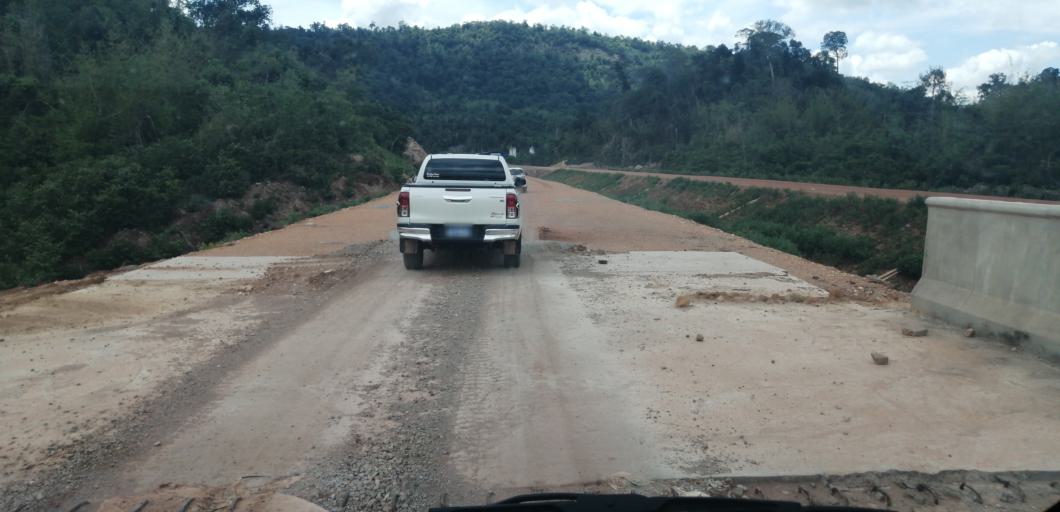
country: LA
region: Vientiane
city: Muang Phon-Hong
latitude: 18.5439
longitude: 102.3663
